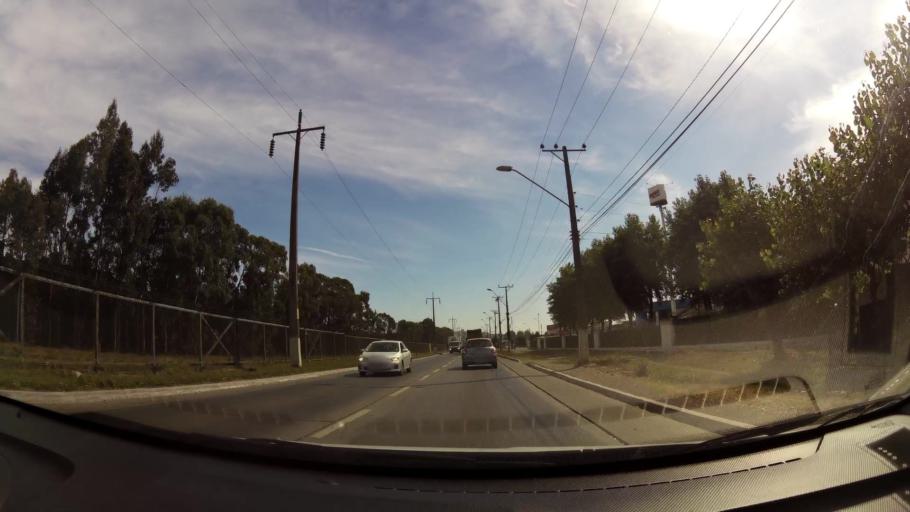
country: CL
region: Biobio
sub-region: Provincia de Concepcion
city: Talcahuano
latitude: -36.7351
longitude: -73.1199
